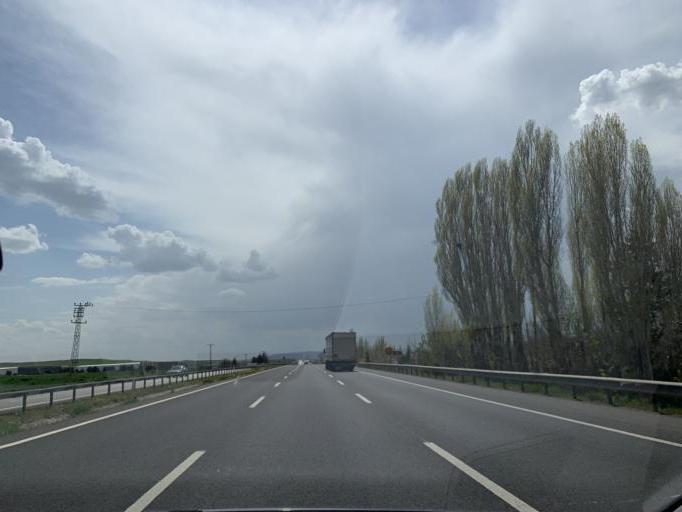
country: TR
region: Ankara
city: Temelli
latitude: 39.6920
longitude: 32.2560
